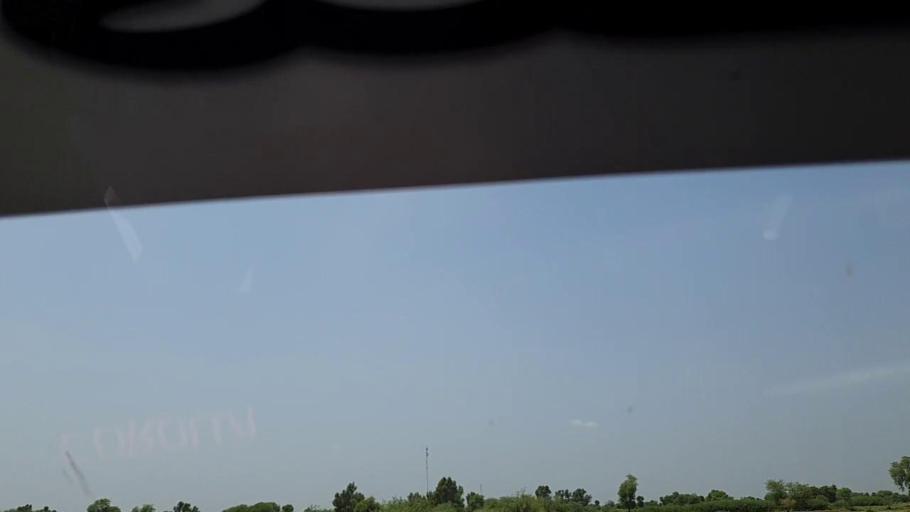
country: PK
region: Sindh
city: Adilpur
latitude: 27.9153
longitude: 69.2084
